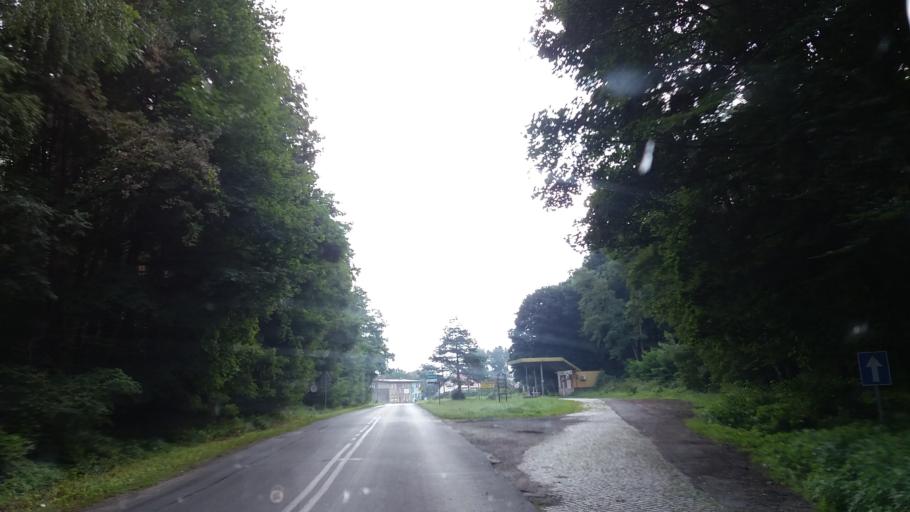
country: PL
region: West Pomeranian Voivodeship
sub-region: Powiat choszczenski
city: Krzecin
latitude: 53.0856
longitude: 15.4787
